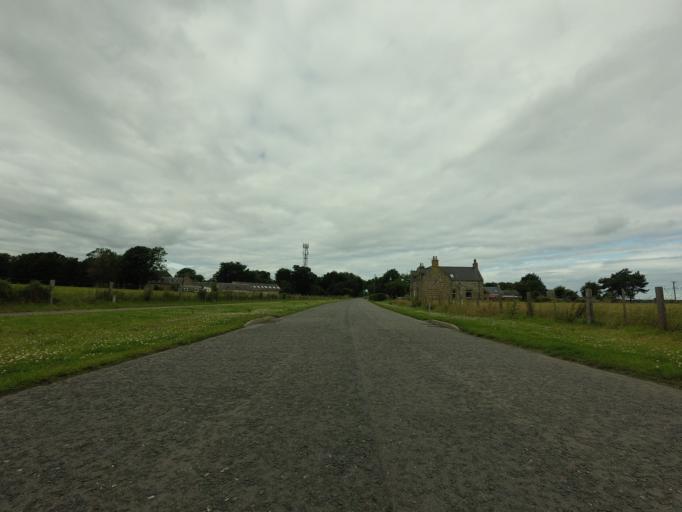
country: GB
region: Scotland
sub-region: Moray
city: Forres
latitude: 57.6147
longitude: -3.6277
